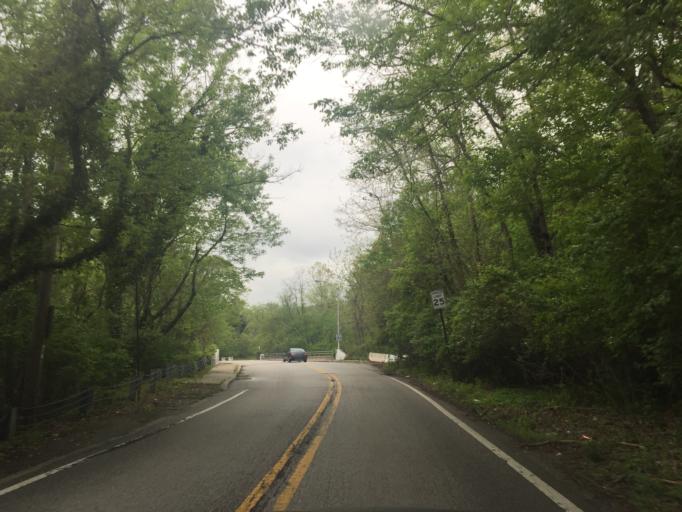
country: US
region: Maryland
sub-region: Baltimore County
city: Charlestown
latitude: 39.3053
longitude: -76.6783
